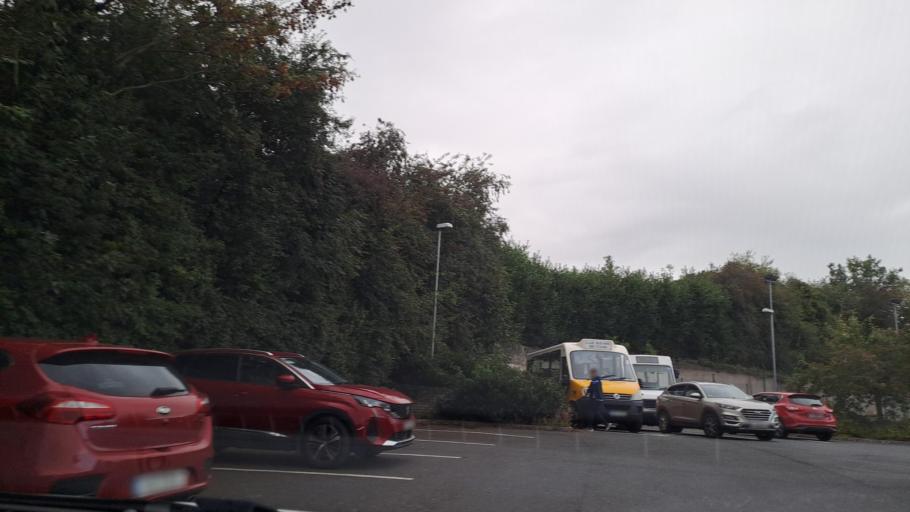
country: IE
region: Ulster
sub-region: County Monaghan
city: Monaghan
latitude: 54.2456
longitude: -6.9787
